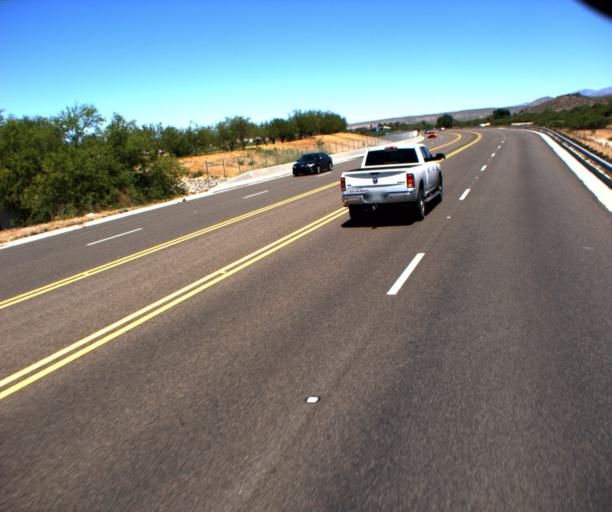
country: US
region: Arizona
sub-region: Maricopa County
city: Wickenburg
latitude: 33.9791
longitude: -112.7336
